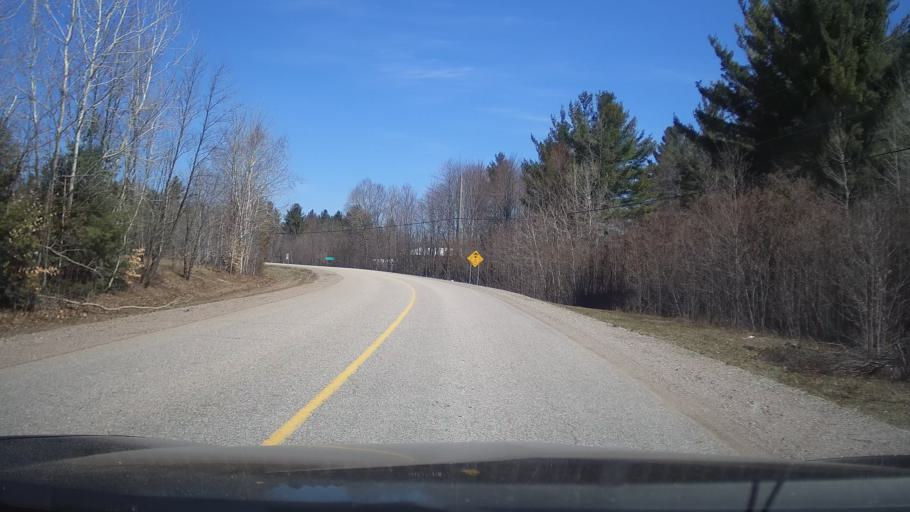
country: CA
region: Ontario
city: Arnprior
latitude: 45.5427
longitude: -76.3653
